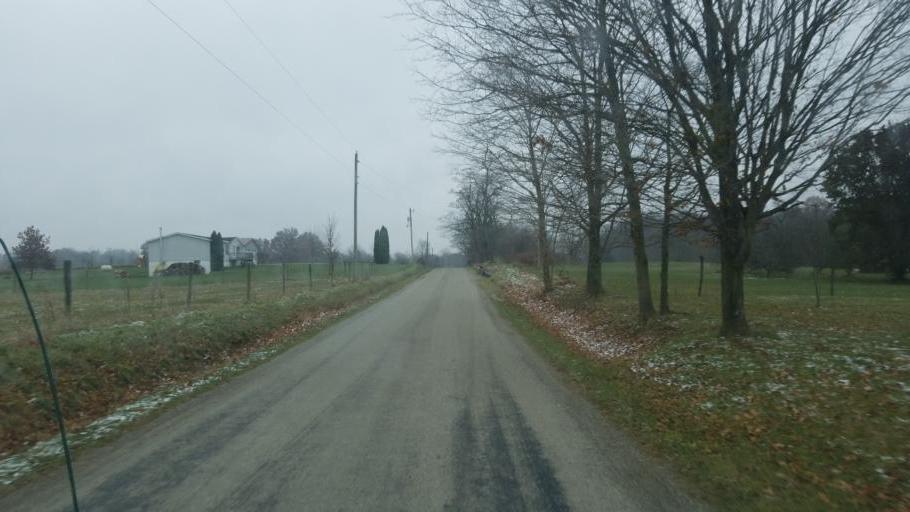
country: US
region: Ohio
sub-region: Huron County
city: New London
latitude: 40.9755
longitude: -82.3733
